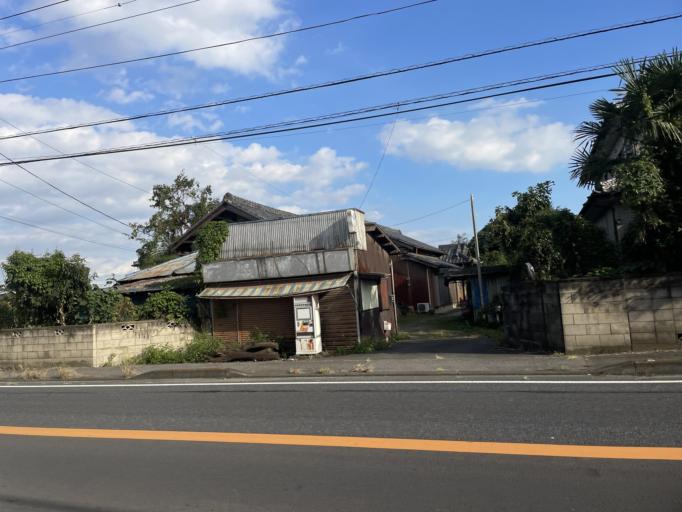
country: JP
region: Tochigi
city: Oyama
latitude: 36.2819
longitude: 139.7770
